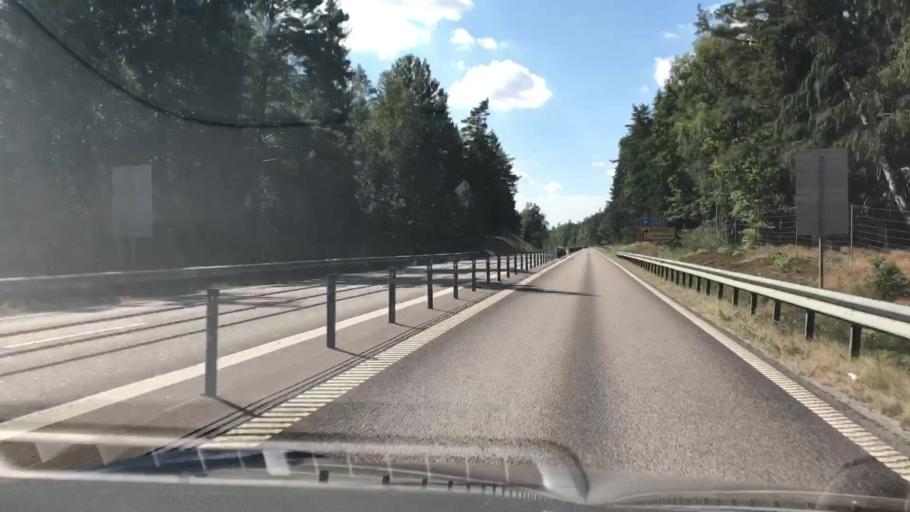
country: SE
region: Kalmar
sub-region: Monsteras Kommun
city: Timmernabben
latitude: 56.8647
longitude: 16.3807
